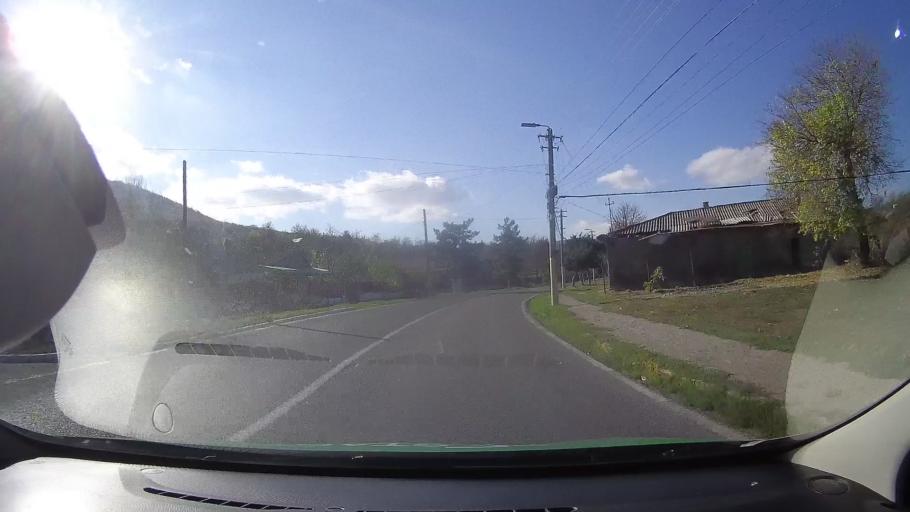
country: RO
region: Tulcea
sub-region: Oras Babadag
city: Babadag
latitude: 44.8840
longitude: 28.7006
